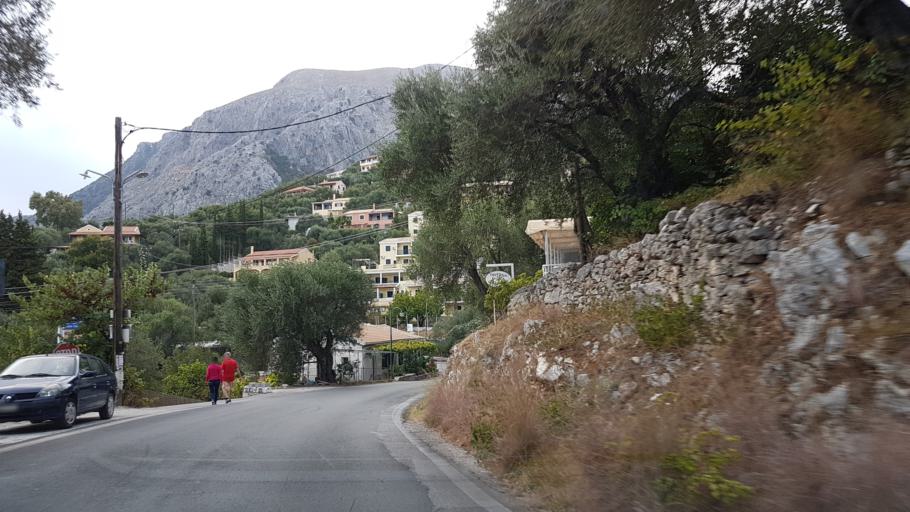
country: GR
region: Ionian Islands
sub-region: Nomos Kerkyras
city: Kontokali
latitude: 39.7253
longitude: 19.8936
